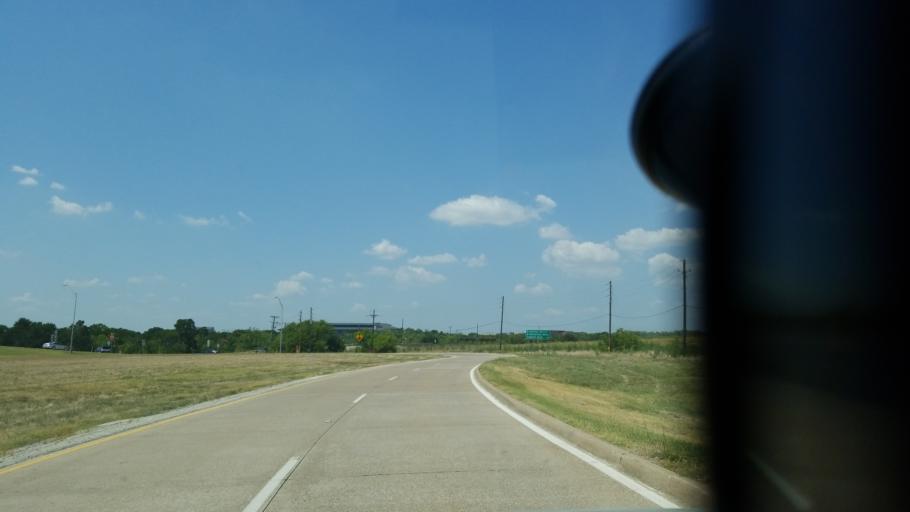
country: US
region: Texas
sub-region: Dallas County
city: Farmers Branch
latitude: 32.8815
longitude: -96.9455
